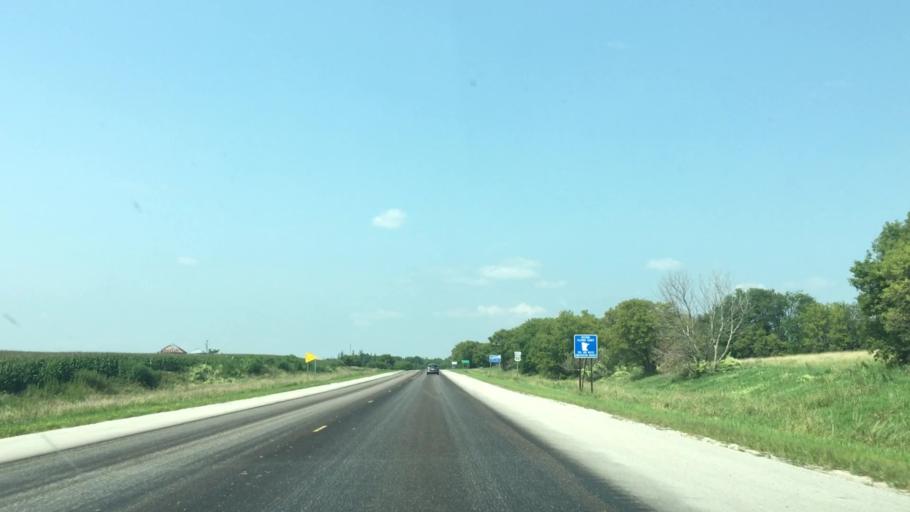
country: US
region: Minnesota
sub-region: Fillmore County
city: Harmony
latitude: 43.5012
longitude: -91.8711
